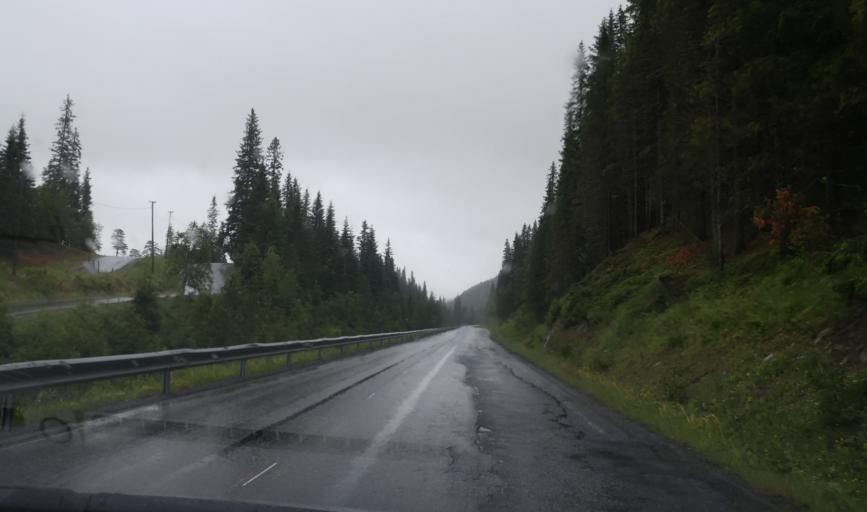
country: NO
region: Sor-Trondelag
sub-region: Selbu
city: Mebonden
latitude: 63.3341
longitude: 11.0928
